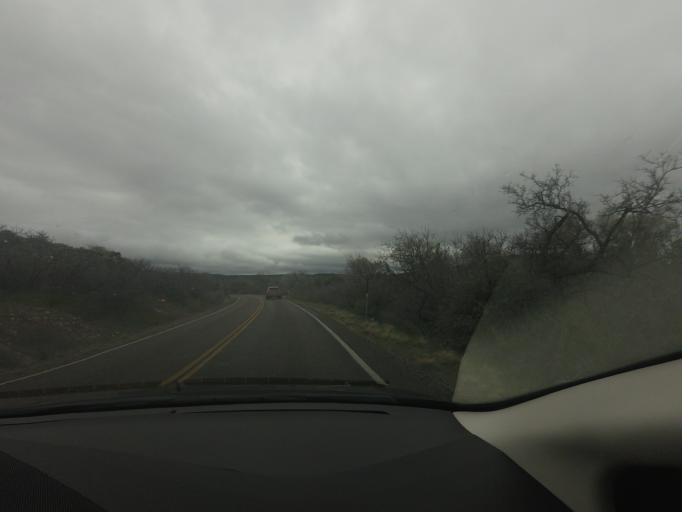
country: US
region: Arizona
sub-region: Yavapai County
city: Lake Montezuma
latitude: 34.6483
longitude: -111.7656
